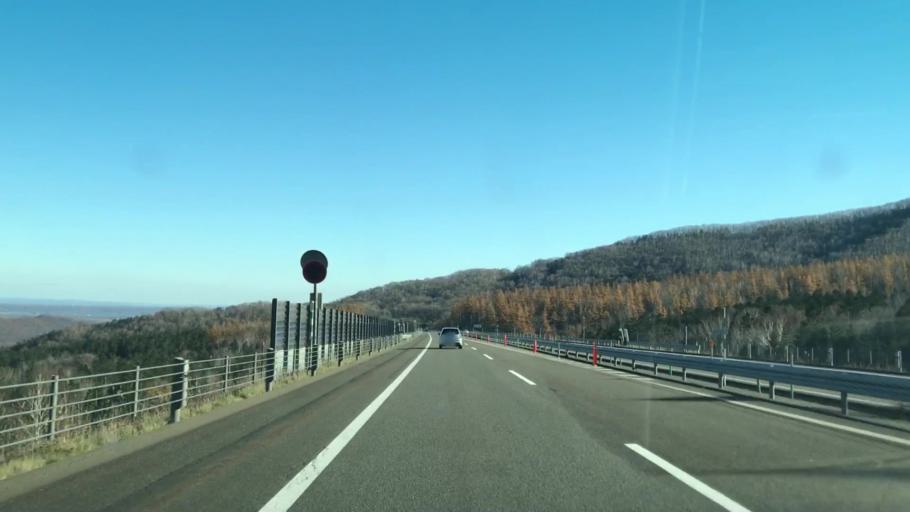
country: JP
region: Hokkaido
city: Otofuke
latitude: 43.0662
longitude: 142.7673
